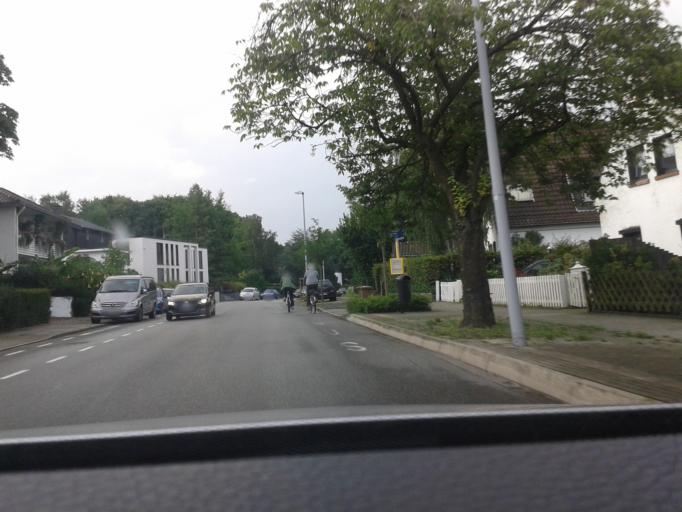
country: DE
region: North Rhine-Westphalia
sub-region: Regierungsbezirk Dusseldorf
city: Muelheim (Ruhr)
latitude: 51.4213
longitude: 6.8250
